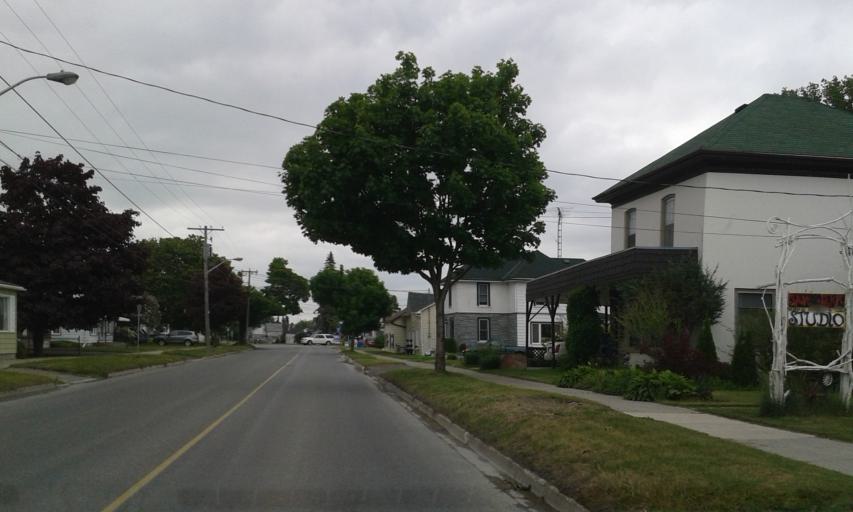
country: CA
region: Ontario
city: Prince Edward
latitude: 43.9520
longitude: -77.3409
